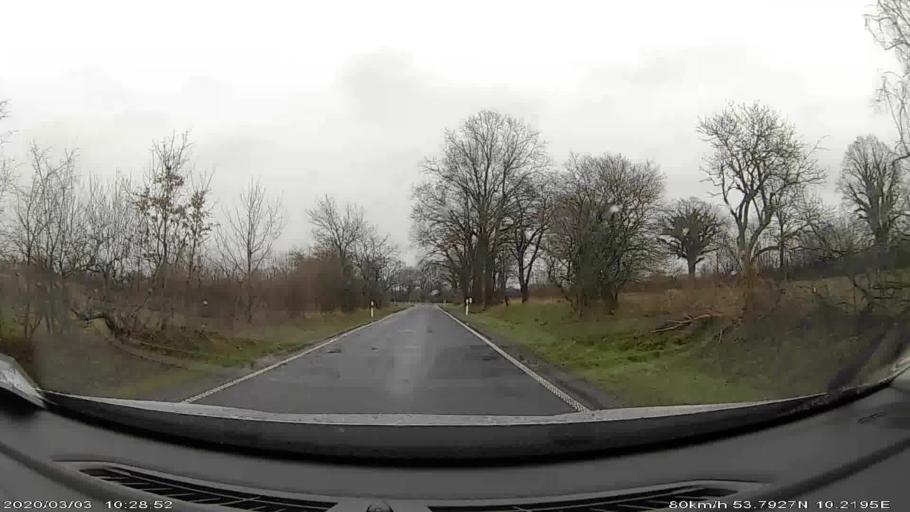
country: DE
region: Schleswig-Holstein
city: Sulfeld
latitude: 53.7948
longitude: 10.2240
